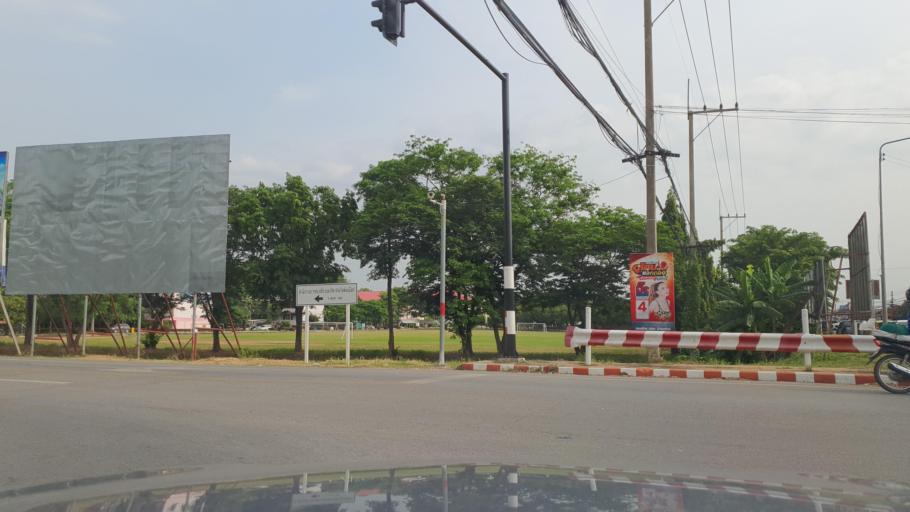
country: TH
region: Phitsanulok
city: Phitsanulok
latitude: 16.8424
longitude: 100.2656
